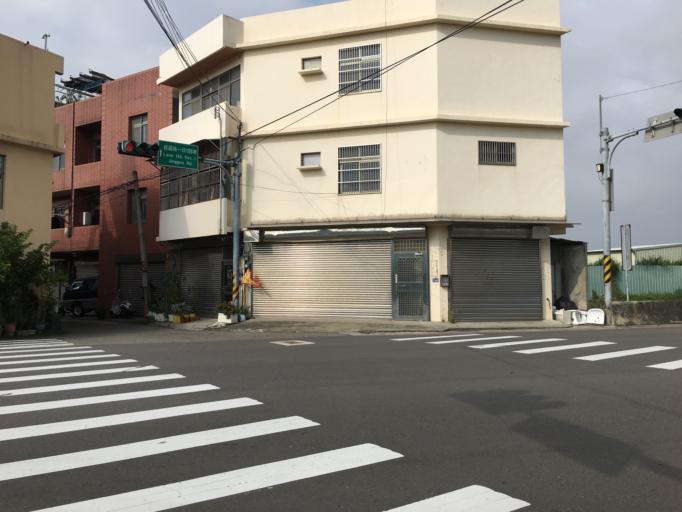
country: TW
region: Taiwan
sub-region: Hsinchu
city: Hsinchu
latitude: 24.8172
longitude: 120.9890
